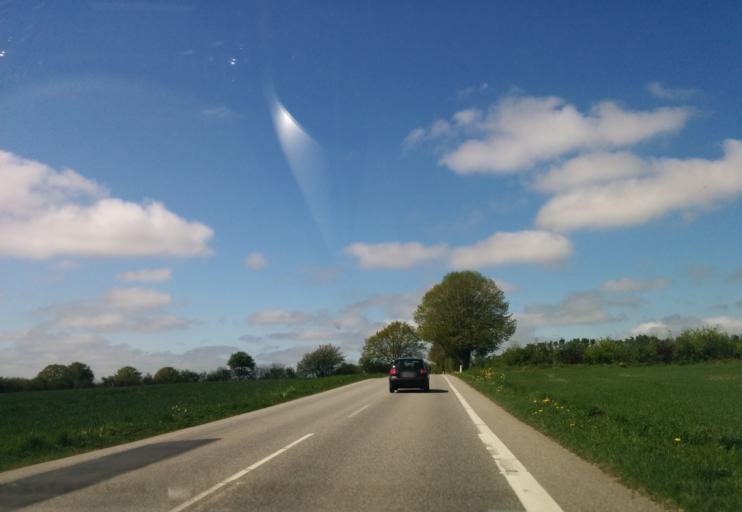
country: DK
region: South Denmark
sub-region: Assens Kommune
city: Tommerup
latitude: 55.3228
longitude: 10.2299
